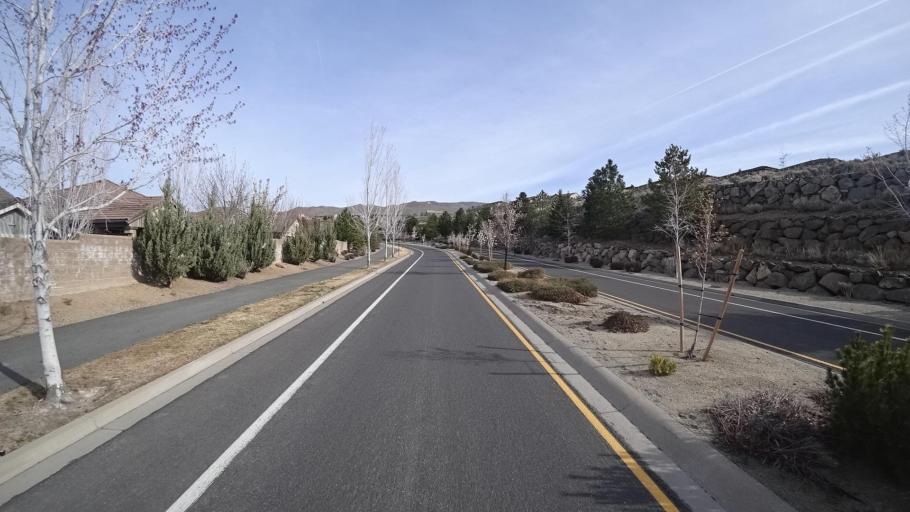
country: US
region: Nevada
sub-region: Washoe County
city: Mogul
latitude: 39.5243
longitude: -119.9459
